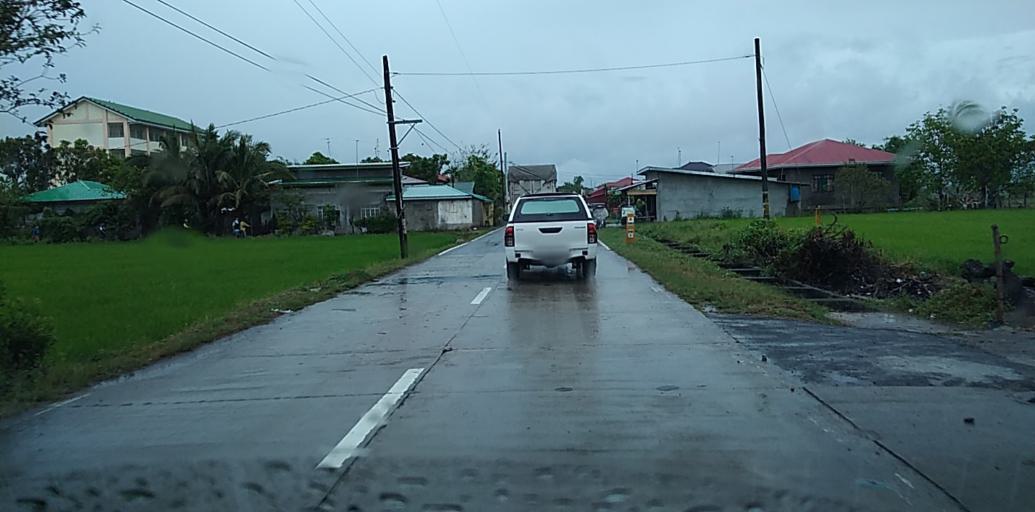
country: PH
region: Central Luzon
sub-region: Province of Pampanga
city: Salapungan
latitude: 15.1351
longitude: 120.9316
